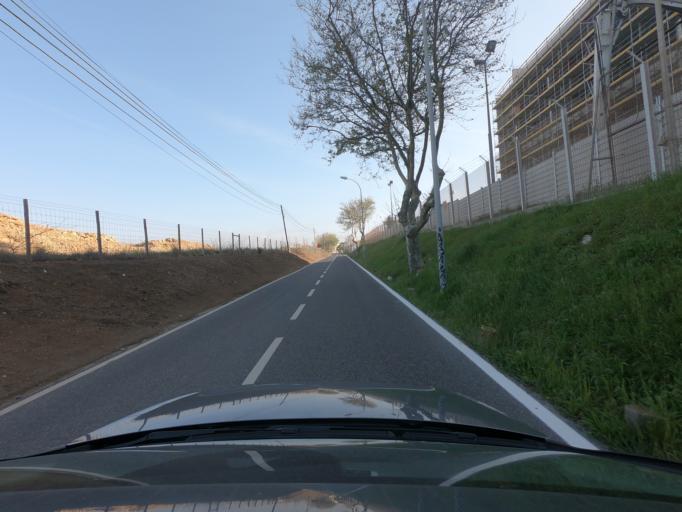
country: PT
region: Lisbon
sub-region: Oeiras
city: Carcavelos
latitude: 38.6783
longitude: -9.3240
